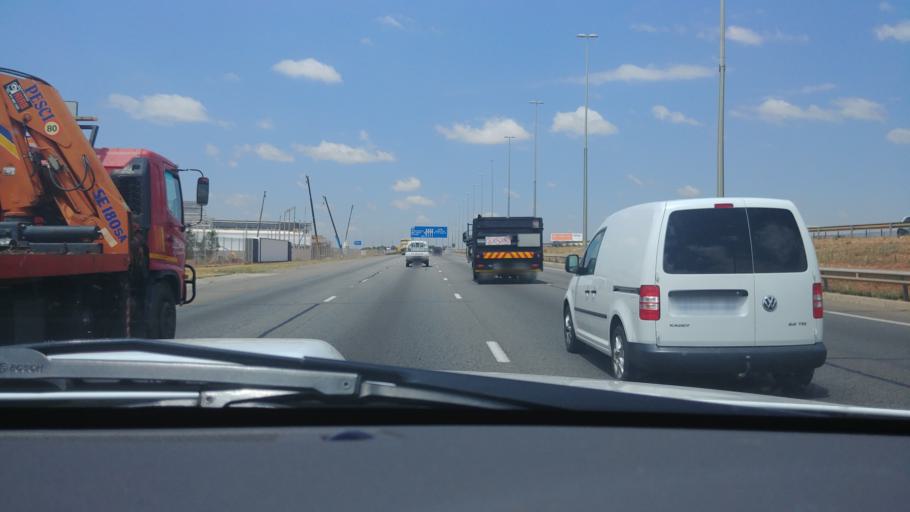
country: ZA
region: Gauteng
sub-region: Ekurhuleni Metropolitan Municipality
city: Tembisa
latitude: -26.0221
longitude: 28.2612
